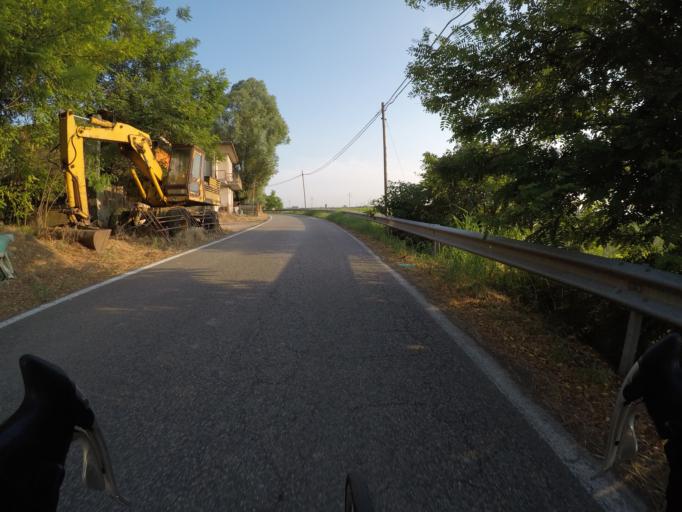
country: IT
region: Veneto
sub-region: Provincia di Rovigo
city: Villanova del Ghebbo Canton
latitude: 45.0513
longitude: 11.6439
